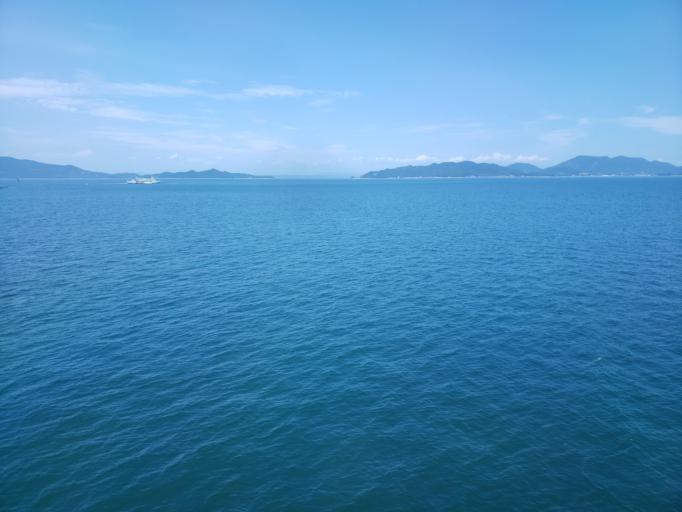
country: JP
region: Kagawa
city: Tonosho
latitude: 34.4055
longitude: 134.1428
